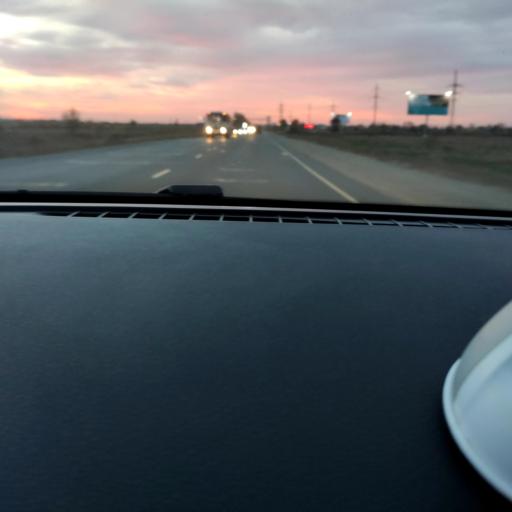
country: RU
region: Samara
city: Samara
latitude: 53.1279
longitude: 50.1632
